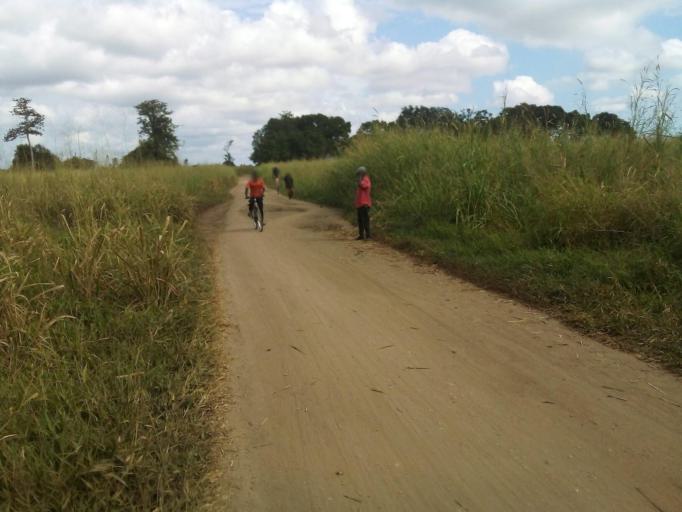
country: MZ
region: Zambezia
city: Quelimane
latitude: -17.5521
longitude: 36.6972
